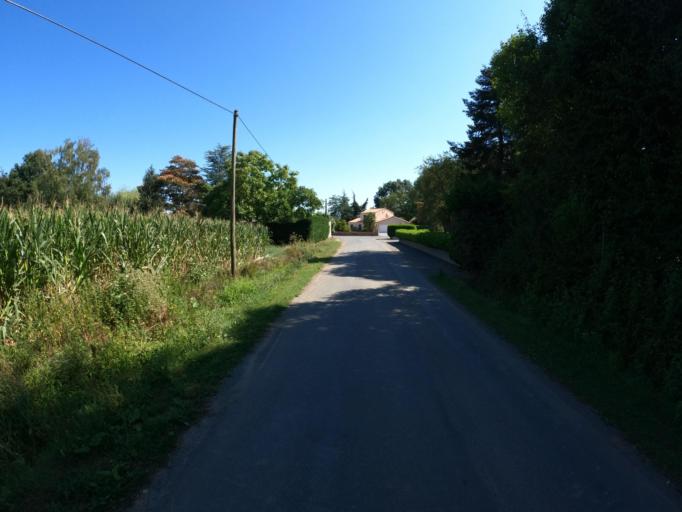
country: FR
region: Pays de la Loire
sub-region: Departement de la Vendee
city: Bouffere
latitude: 46.9701
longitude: -1.3568
